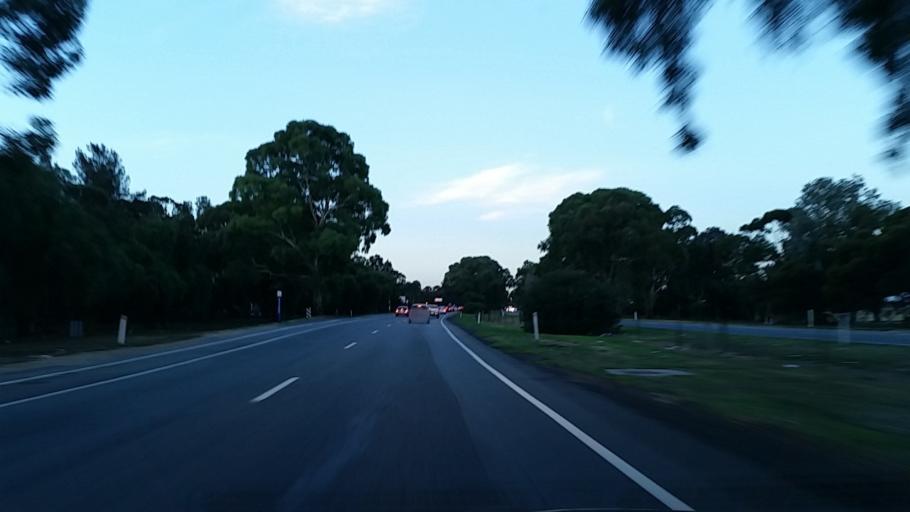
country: AU
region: South Australia
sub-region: Salisbury
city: Salisbury
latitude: -34.7886
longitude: 138.6496
